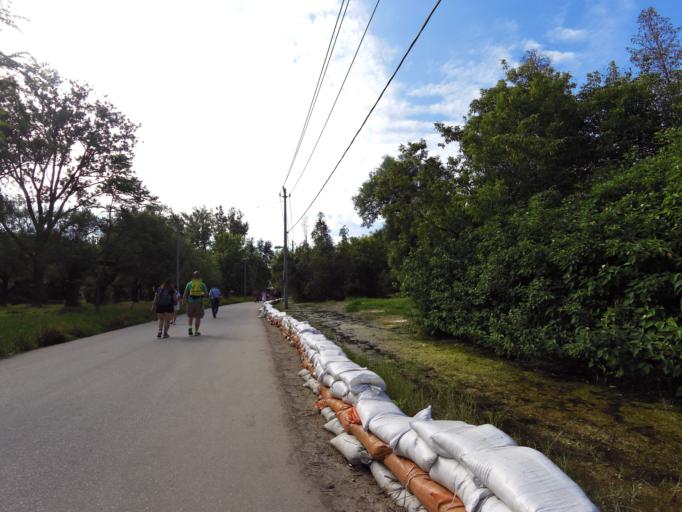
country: CA
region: Ontario
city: Toronto
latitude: 43.6302
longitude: -79.3565
